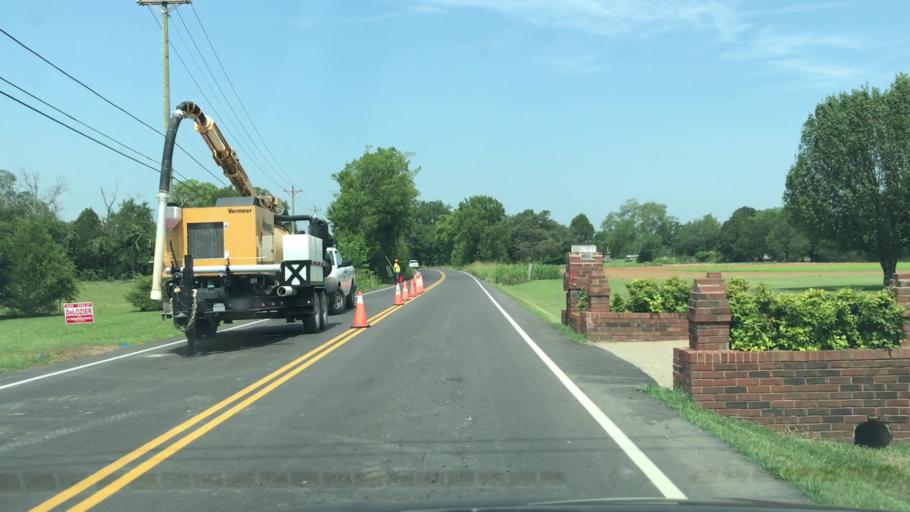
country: US
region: Tennessee
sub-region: Wilson County
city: Rural Hill
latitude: 36.1136
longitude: -86.4322
